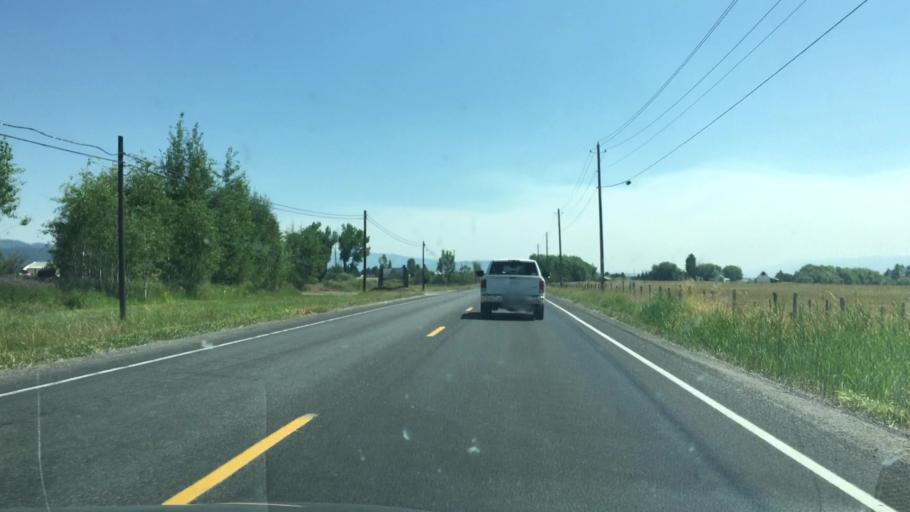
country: US
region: Idaho
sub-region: Valley County
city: McCall
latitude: 44.8468
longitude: -116.0894
